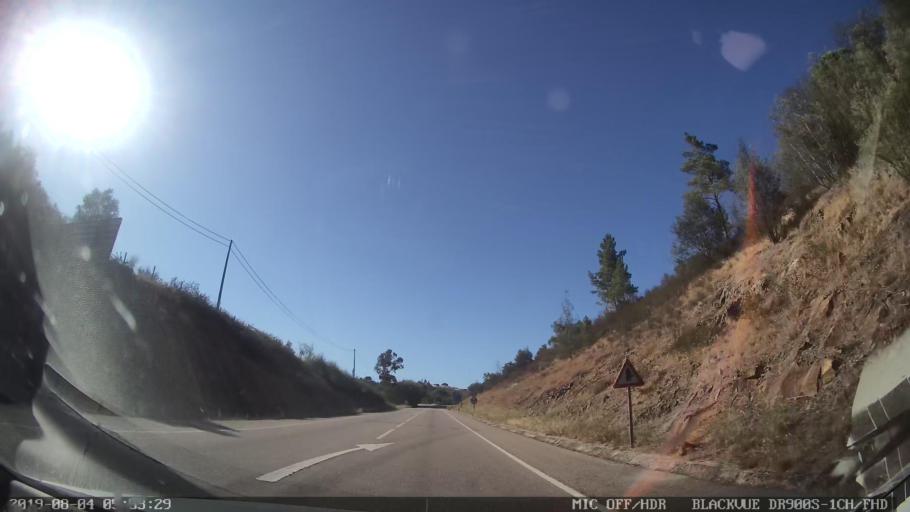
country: PT
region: Portalegre
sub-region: Gaviao
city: Gaviao
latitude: 39.4547
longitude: -7.9297
